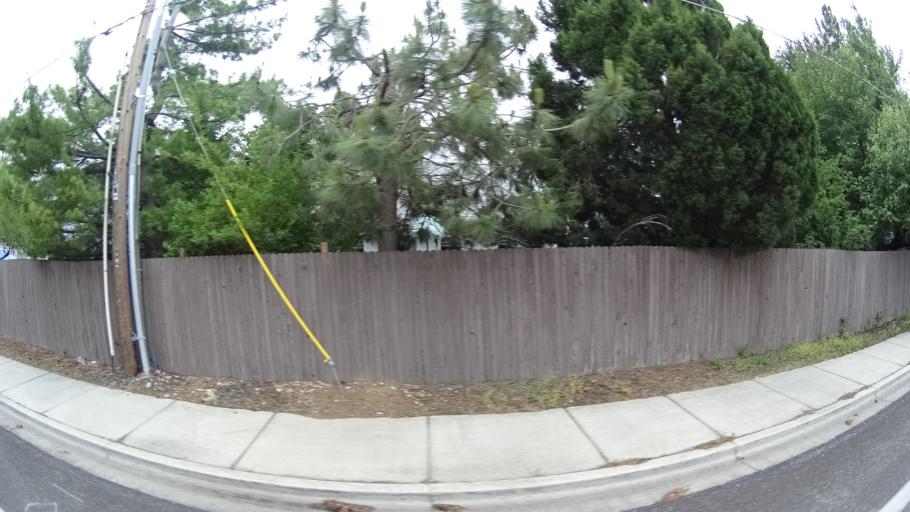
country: US
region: Idaho
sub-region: Ada County
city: Eagle
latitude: 43.6484
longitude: -116.3128
